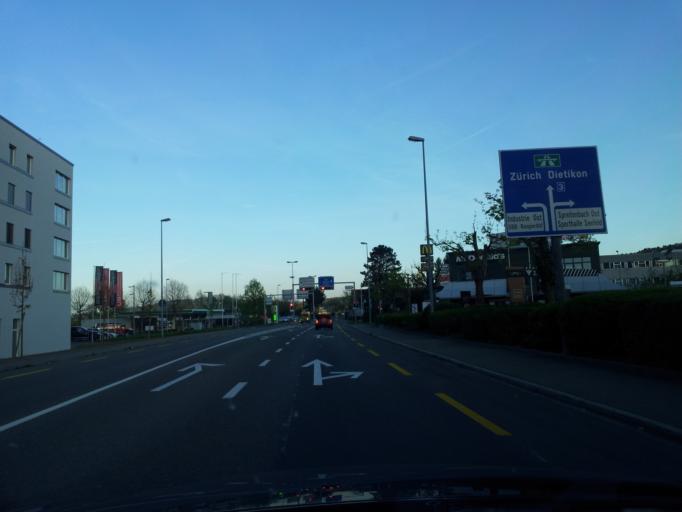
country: CH
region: Aargau
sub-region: Bezirk Baden
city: Spreitenbach
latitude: 47.4192
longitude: 8.3735
